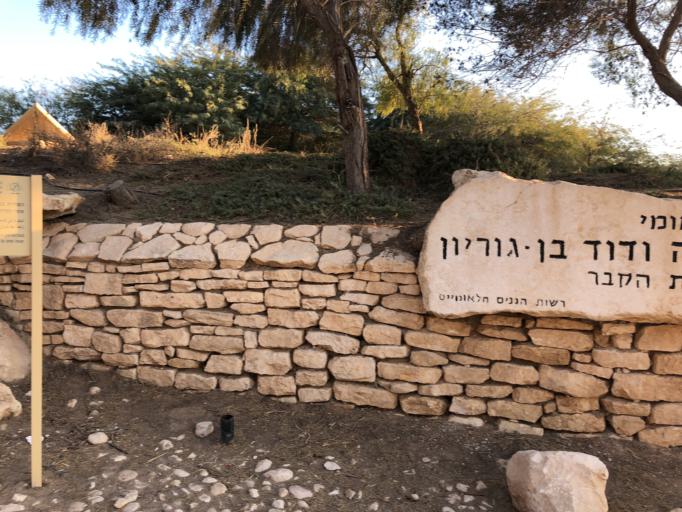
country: IL
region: Southern District
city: Midreshet Ben-Gurion
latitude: 30.8490
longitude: 34.7795
